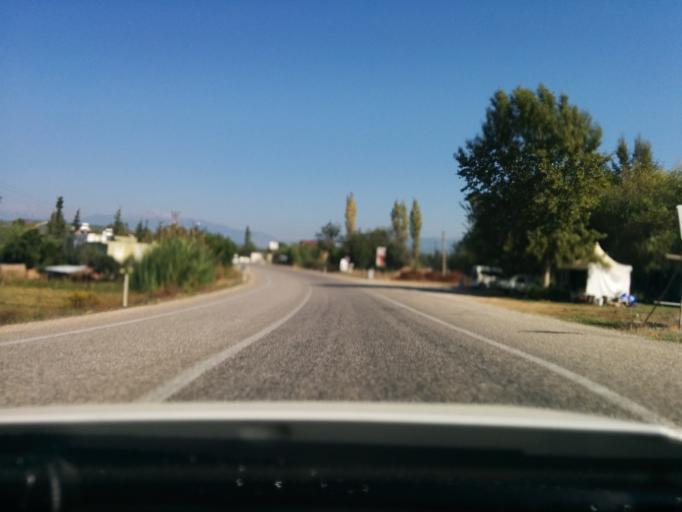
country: TR
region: Mugla
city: Kemer
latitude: 36.5783
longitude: 29.3510
